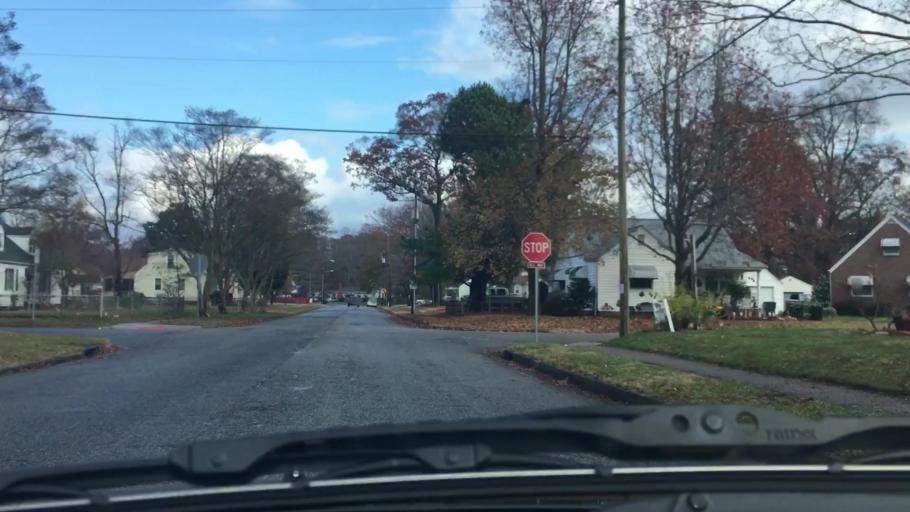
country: US
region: Virginia
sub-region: City of Norfolk
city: Norfolk
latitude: 36.9202
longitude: -76.2486
